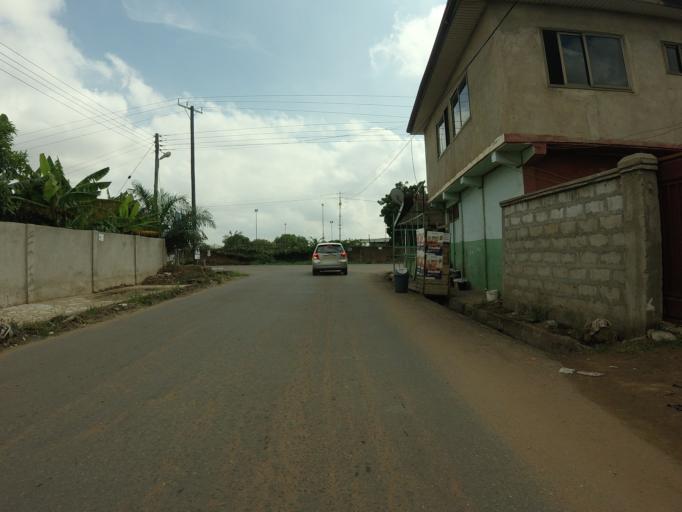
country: GH
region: Greater Accra
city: Nungua
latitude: 5.6060
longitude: -0.0861
